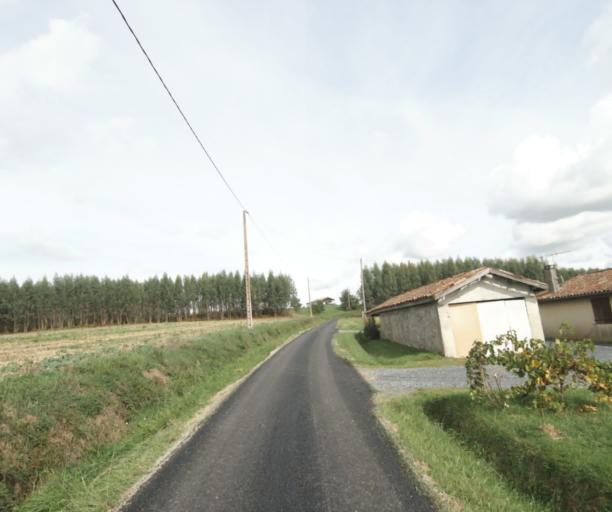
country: FR
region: Midi-Pyrenees
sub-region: Departement du Gers
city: Eauze
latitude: 43.8464
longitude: 0.0761
